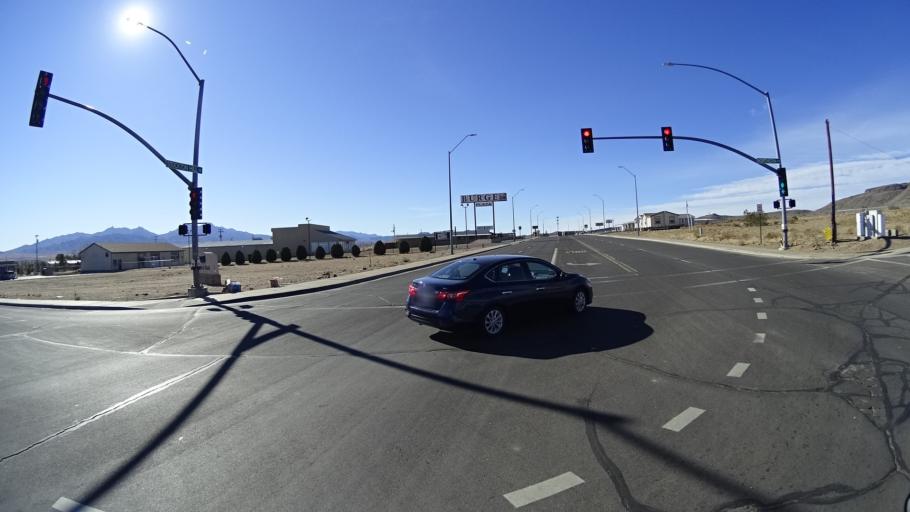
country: US
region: Arizona
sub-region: Mohave County
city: New Kingman-Butler
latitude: 35.2540
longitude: -114.0380
